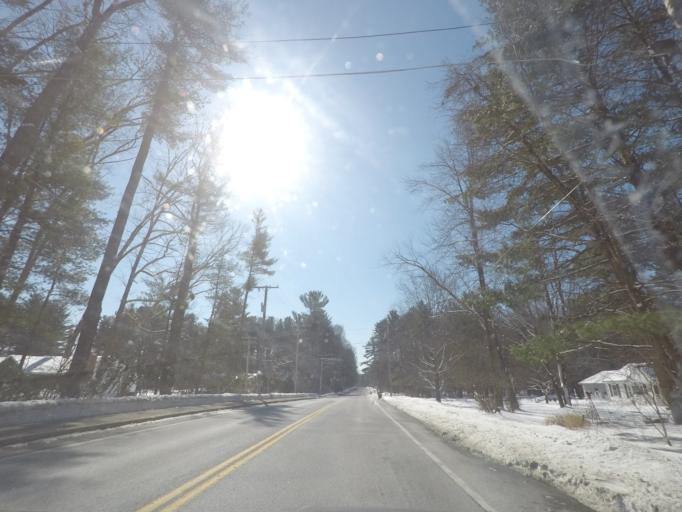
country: US
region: New York
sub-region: Saratoga County
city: Country Knolls
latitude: 42.9152
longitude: -73.8220
